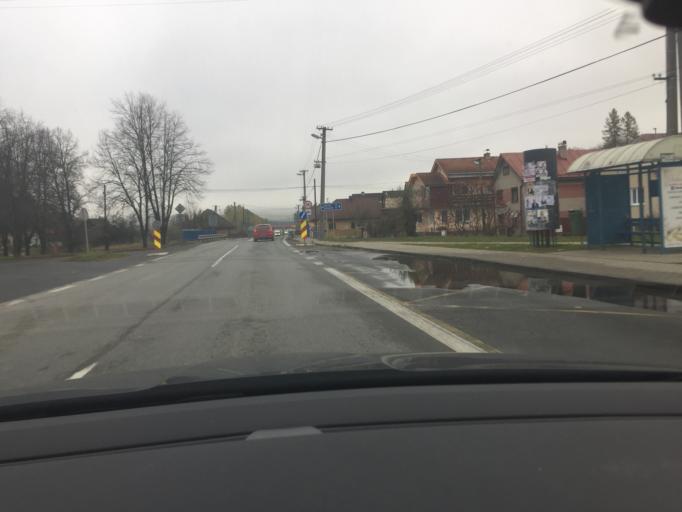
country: SK
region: Presovsky
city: Stara L'ubovna
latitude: 49.2746
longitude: 20.7807
